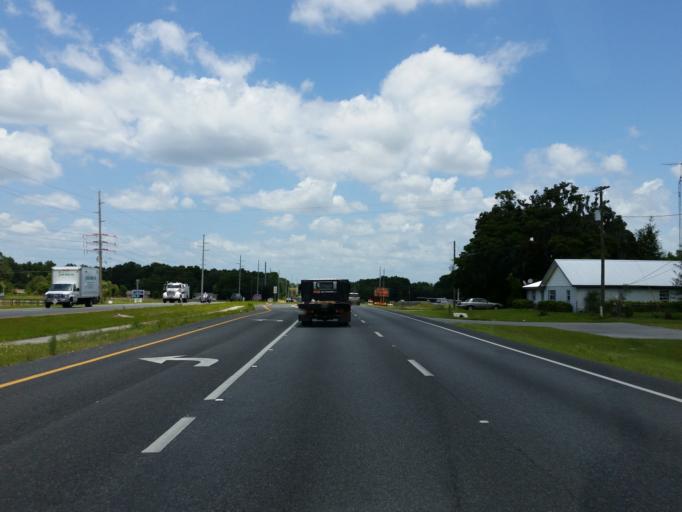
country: US
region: Florida
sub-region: Sumter County
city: The Villages
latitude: 28.9667
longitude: -82.0411
